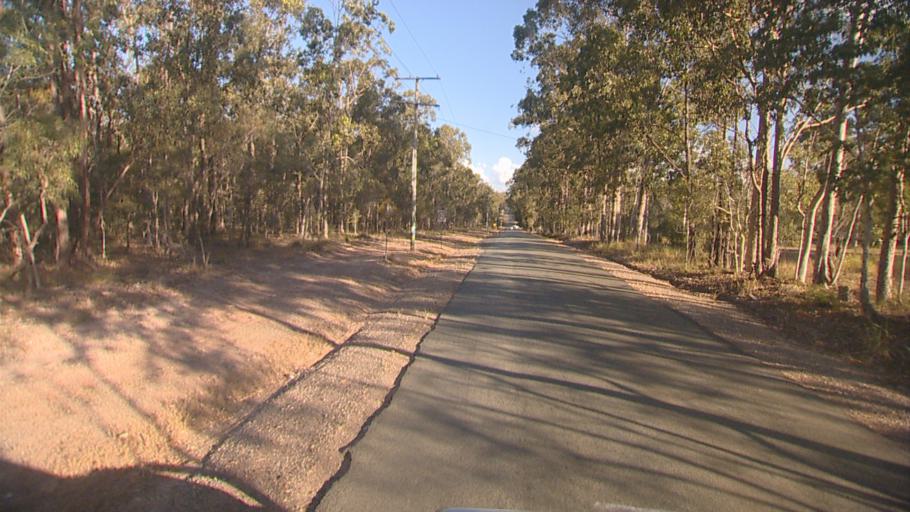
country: AU
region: Queensland
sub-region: Ipswich
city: Springfield Lakes
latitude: -27.7028
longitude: 152.9480
